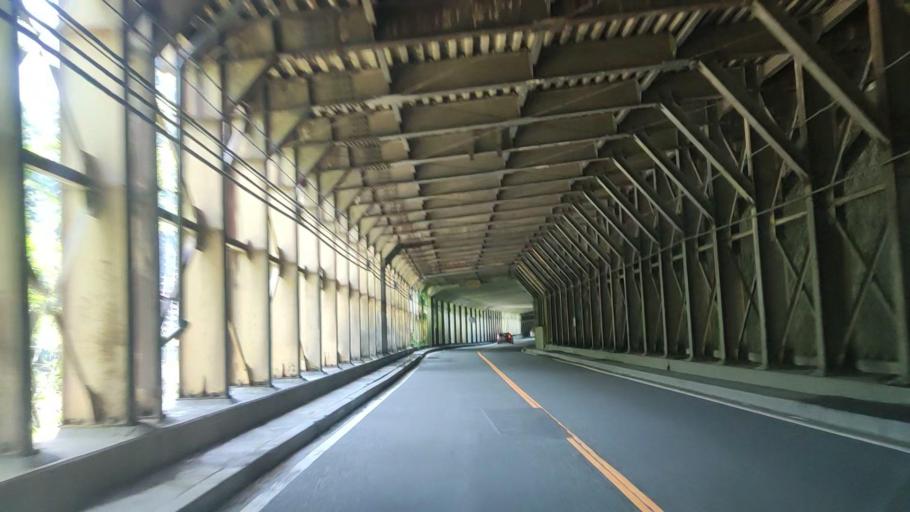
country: JP
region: Niigata
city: Itoigawa
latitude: 36.9095
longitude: 137.8627
